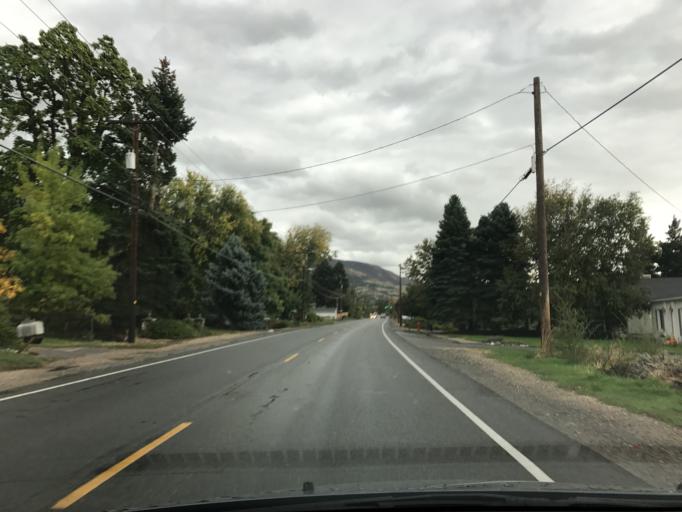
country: US
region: Utah
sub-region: Davis County
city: Farmington
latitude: 40.9946
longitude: -111.8958
